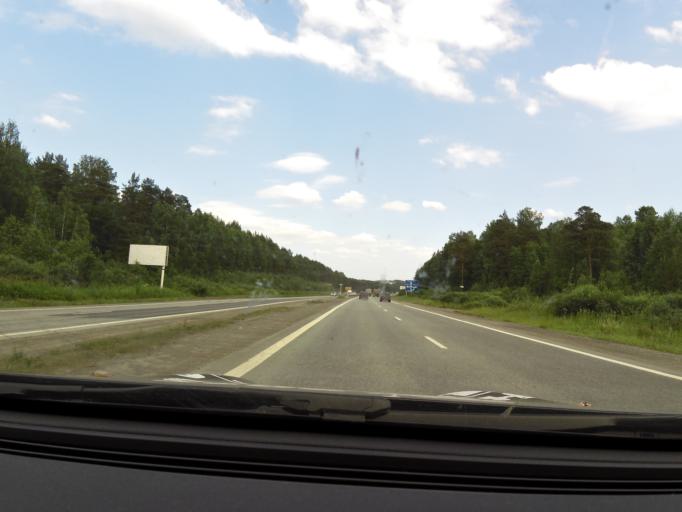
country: RU
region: Sverdlovsk
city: Severka
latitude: 56.8447
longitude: 60.2237
